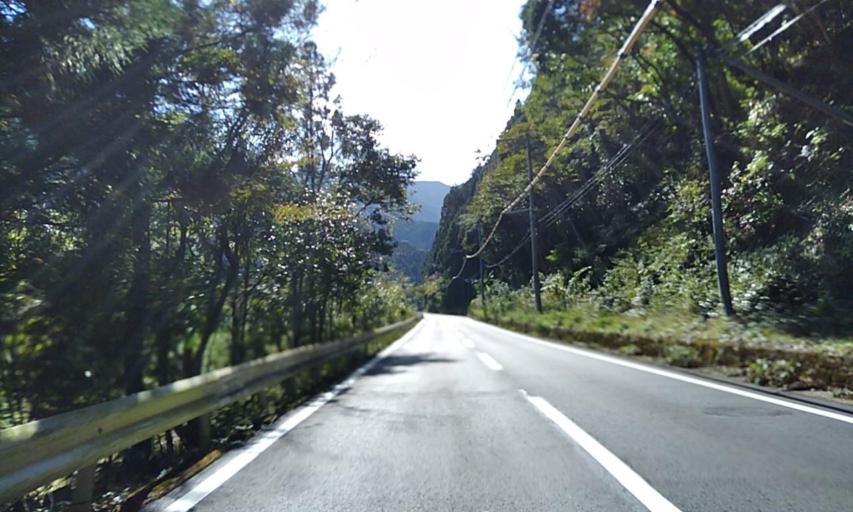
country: JP
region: Wakayama
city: Kainan
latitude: 34.0575
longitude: 135.3534
